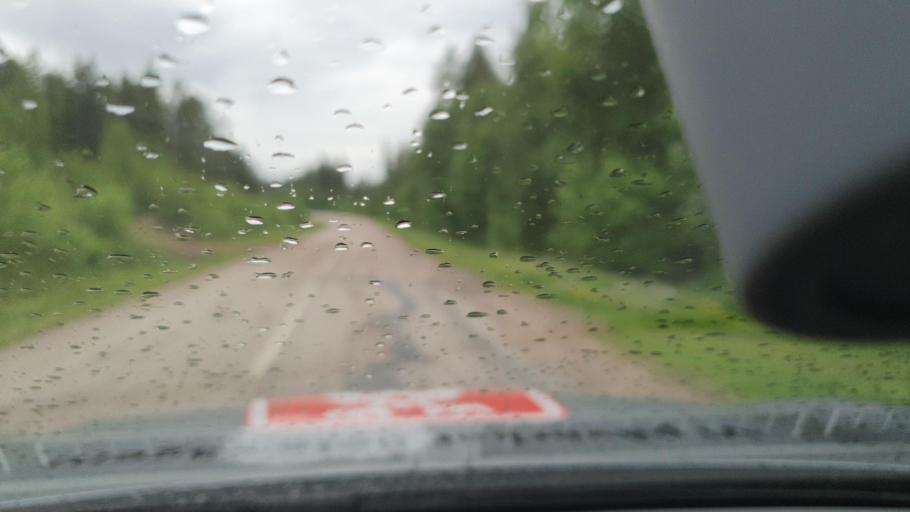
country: SE
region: Norrbotten
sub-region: Overkalix Kommun
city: OEverkalix
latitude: 66.4508
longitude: 22.7709
